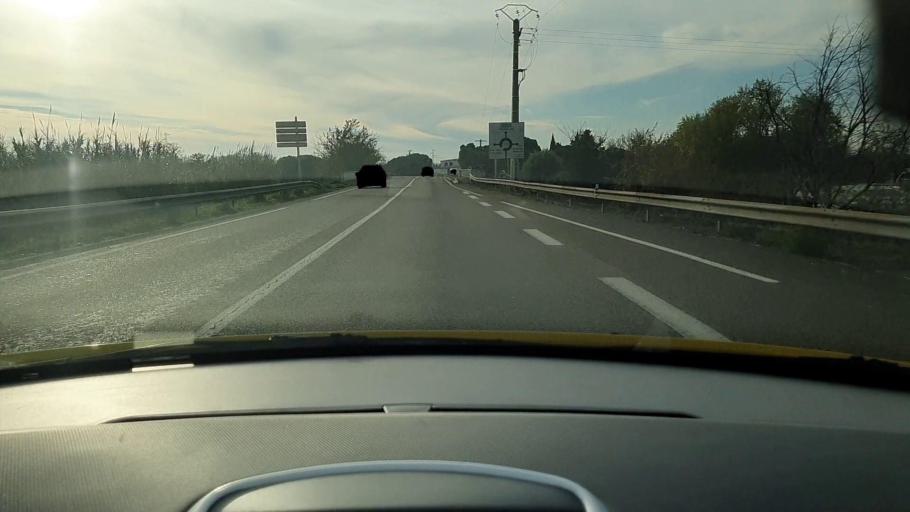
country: FR
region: Languedoc-Roussillon
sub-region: Departement du Gard
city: Bellegarde
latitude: 43.7454
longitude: 4.5213
